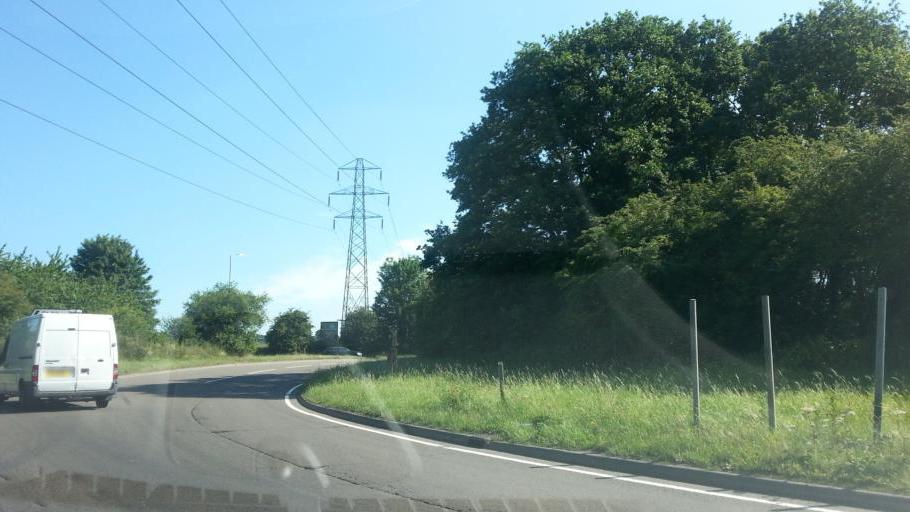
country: GB
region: England
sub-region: Hertfordshire
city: Shenley AV
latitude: 51.7173
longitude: -0.2798
